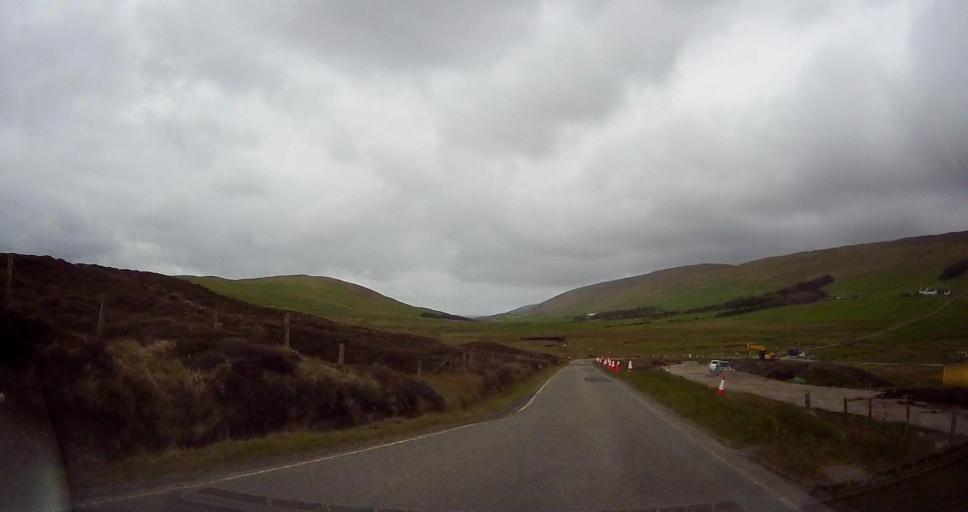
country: GB
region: Scotland
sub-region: Shetland Islands
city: Lerwick
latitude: 60.2767
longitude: -1.2724
